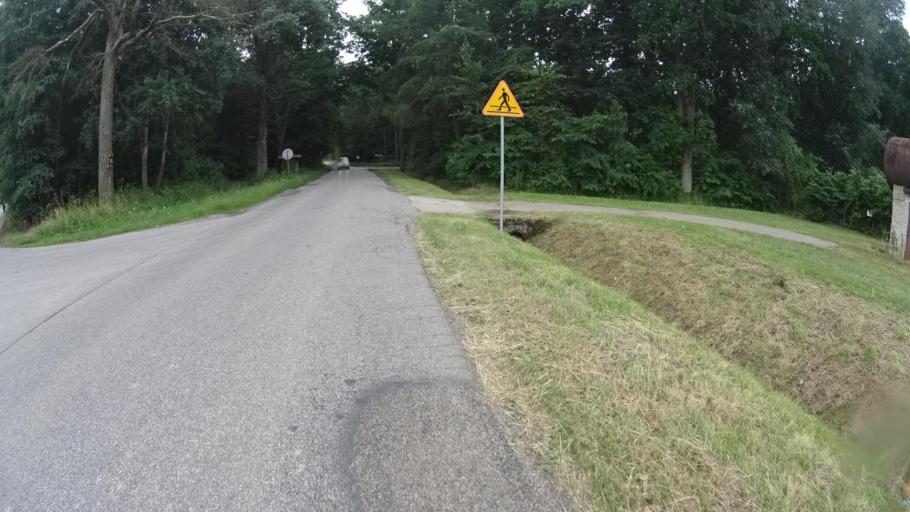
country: PL
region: Masovian Voivodeship
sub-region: Powiat grojecki
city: Goszczyn
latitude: 51.7824
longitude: 20.8542
